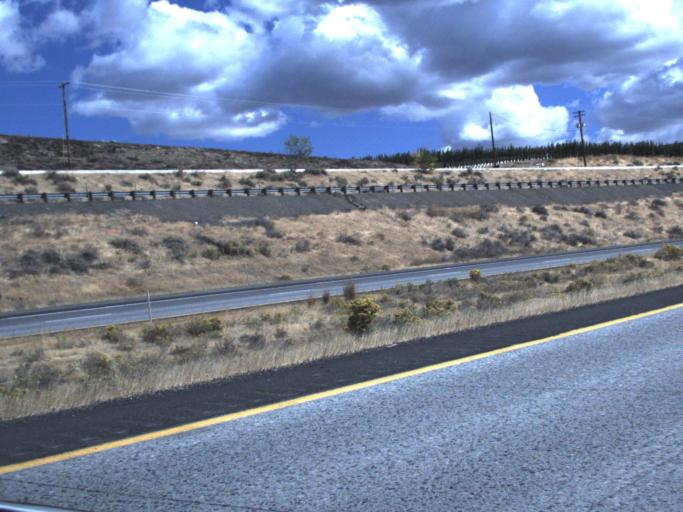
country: US
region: Washington
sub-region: Yakima County
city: Union Gap
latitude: 46.5193
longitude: -120.4592
